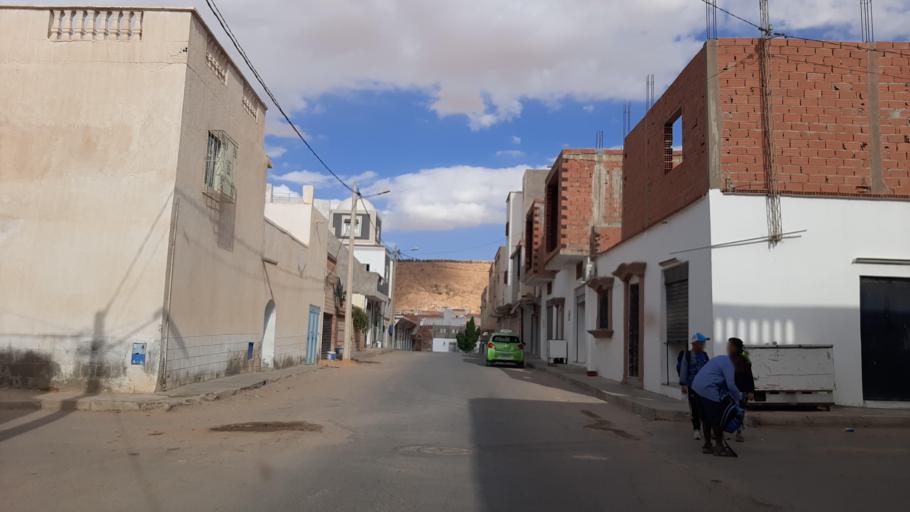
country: TN
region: Tataouine
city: Tataouine
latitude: 32.9292
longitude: 10.4558
